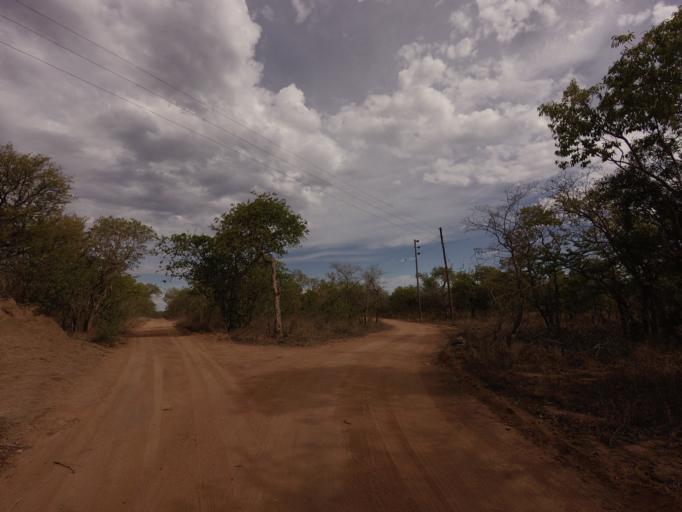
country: ZA
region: Limpopo
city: Thulamahashi
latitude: -24.5202
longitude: 31.1157
